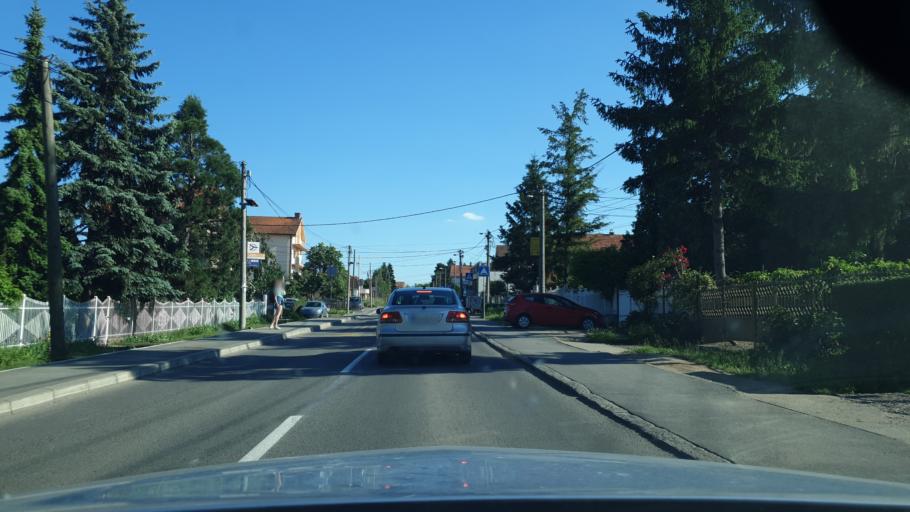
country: RS
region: Central Serbia
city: Sremcica
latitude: 44.7178
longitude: 20.3681
